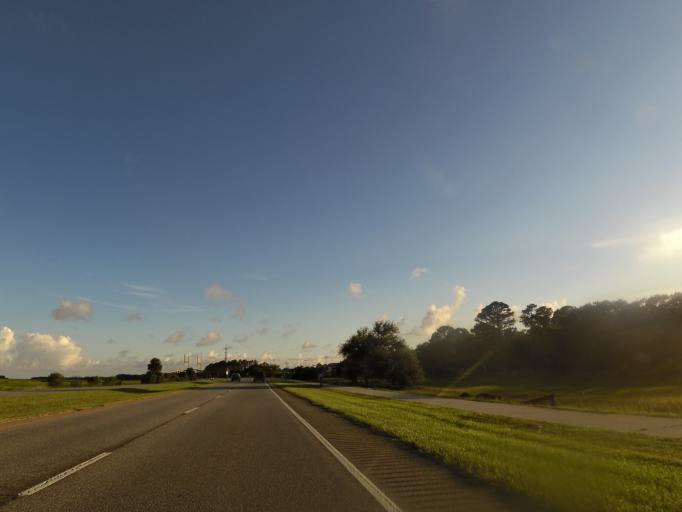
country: US
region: Georgia
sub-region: Glynn County
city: Brunswick
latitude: 31.1439
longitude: -81.4782
